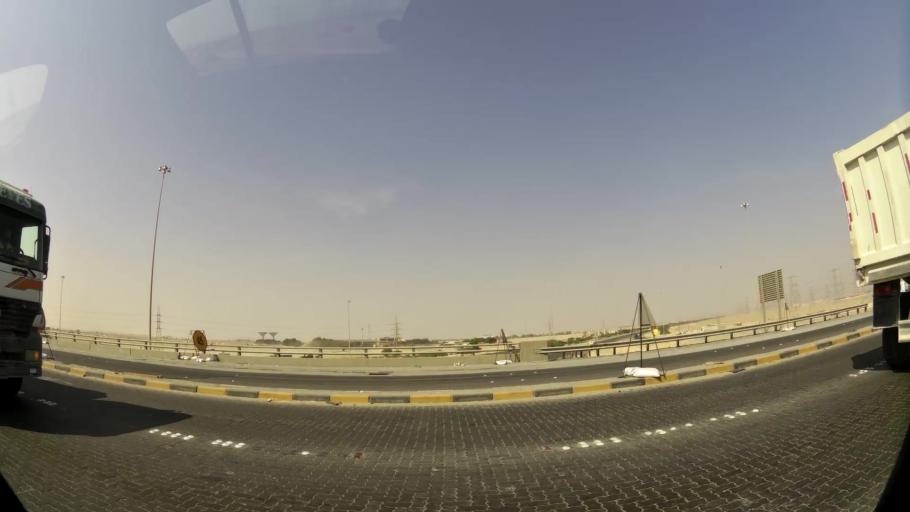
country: KW
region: Al Ahmadi
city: Al Fahahil
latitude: 28.9601
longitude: 48.1227
